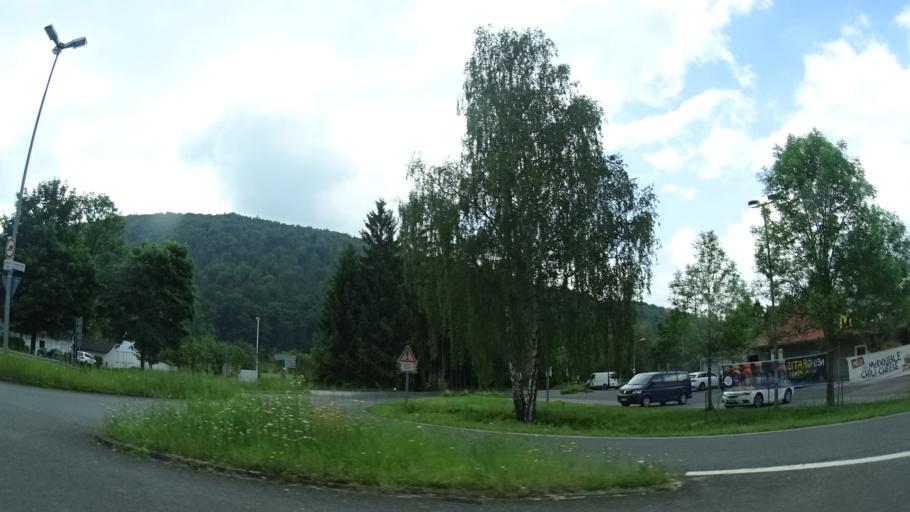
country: DE
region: Bavaria
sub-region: Regierungsbezirk Unterfranken
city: Lohr am Main
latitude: 50.0020
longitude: 9.5849
